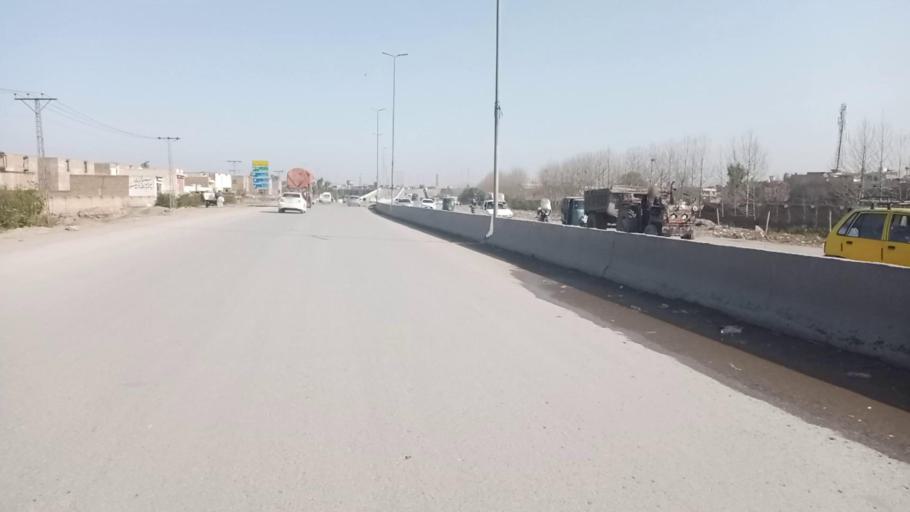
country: PK
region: Khyber Pakhtunkhwa
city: Peshawar
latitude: 34.0334
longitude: 71.5729
